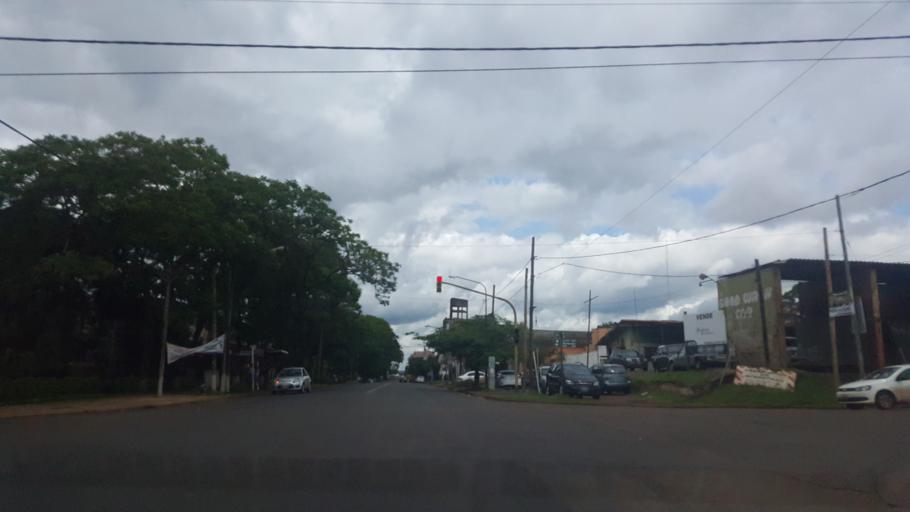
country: AR
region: Misiones
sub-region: Departamento de Capital
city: Posadas
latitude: -27.3933
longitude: -55.9088
